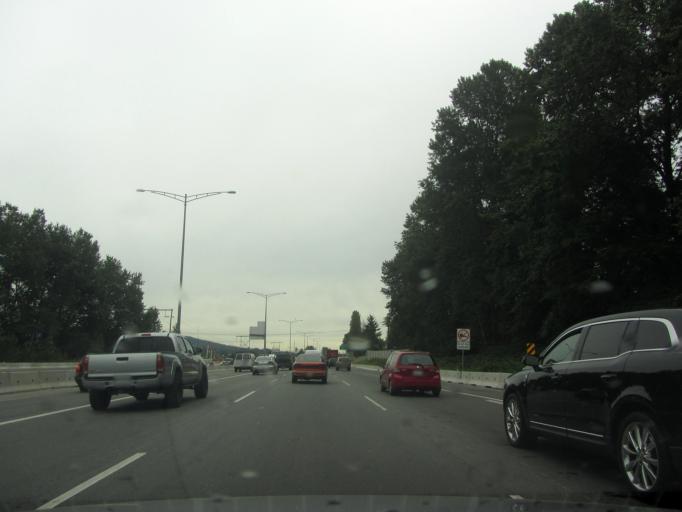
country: CA
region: British Columbia
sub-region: Fraser Valley Regional District
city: North Vancouver
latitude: 49.2625
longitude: -123.0254
